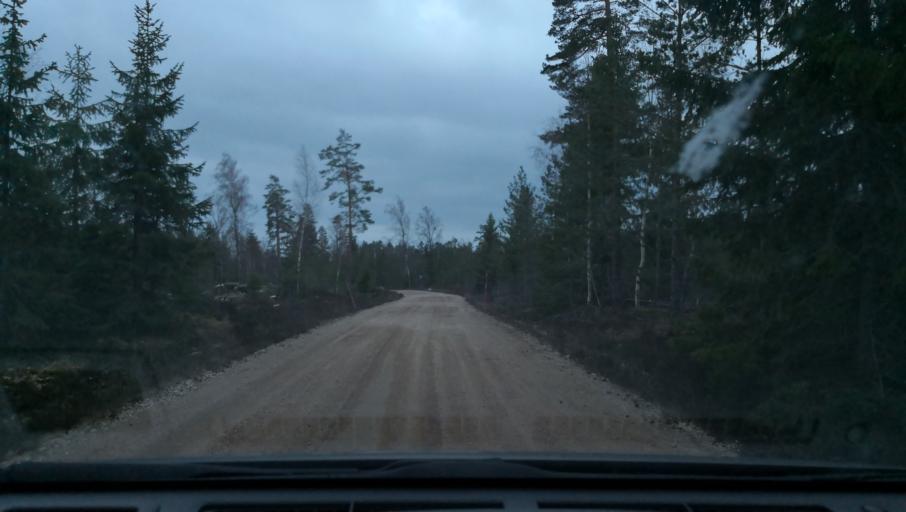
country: SE
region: OErebro
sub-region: Lindesbergs Kommun
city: Fellingsbro
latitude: 59.5923
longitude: 15.5771
